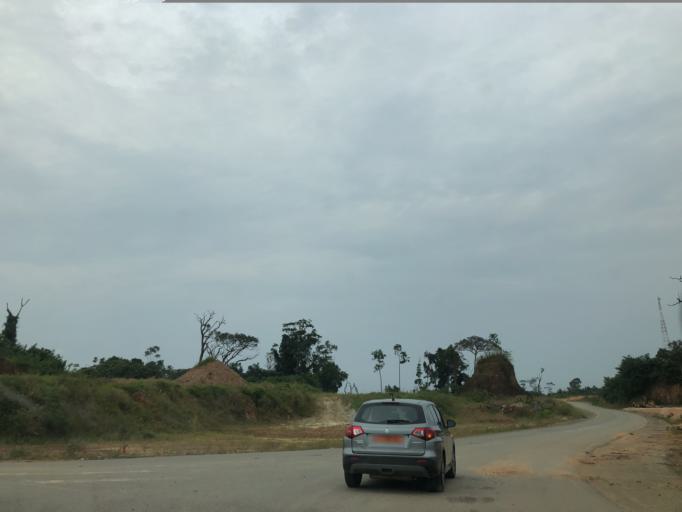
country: CM
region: South Province
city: Kribi
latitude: 2.7172
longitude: 9.8702
